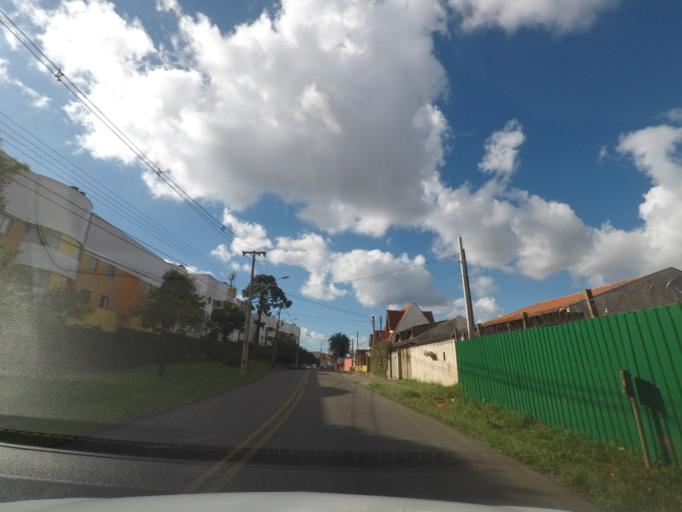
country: BR
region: Parana
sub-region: Curitiba
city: Curitiba
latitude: -25.3796
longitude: -49.2791
